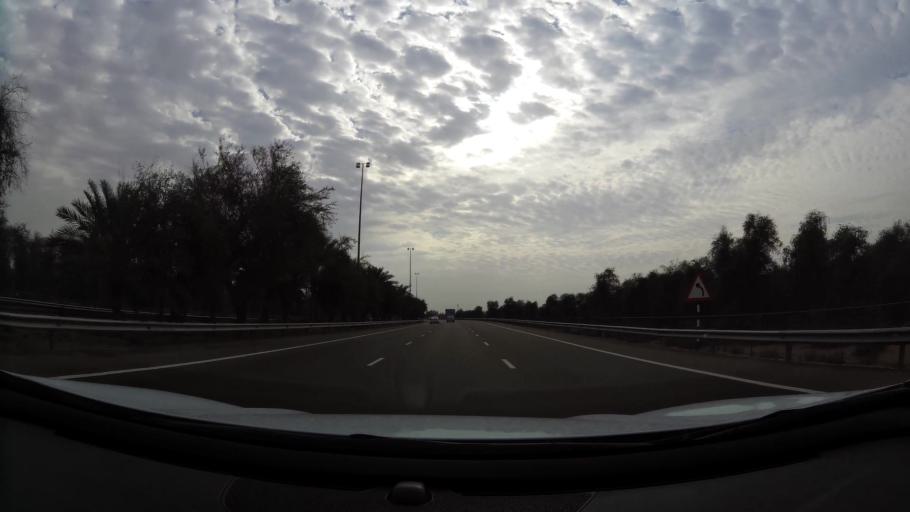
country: AE
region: Abu Dhabi
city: Al Ain
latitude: 24.1681
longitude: 55.2682
